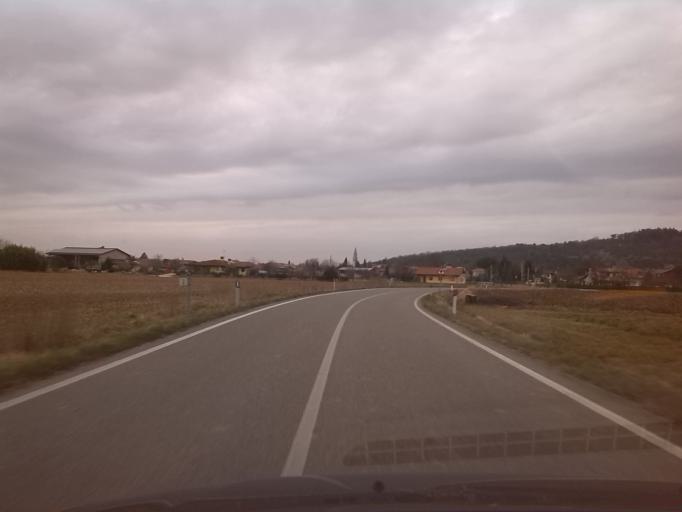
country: IT
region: Friuli Venezia Giulia
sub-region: Provincia di Gorizia
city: Medea
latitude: 45.9134
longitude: 13.4300
